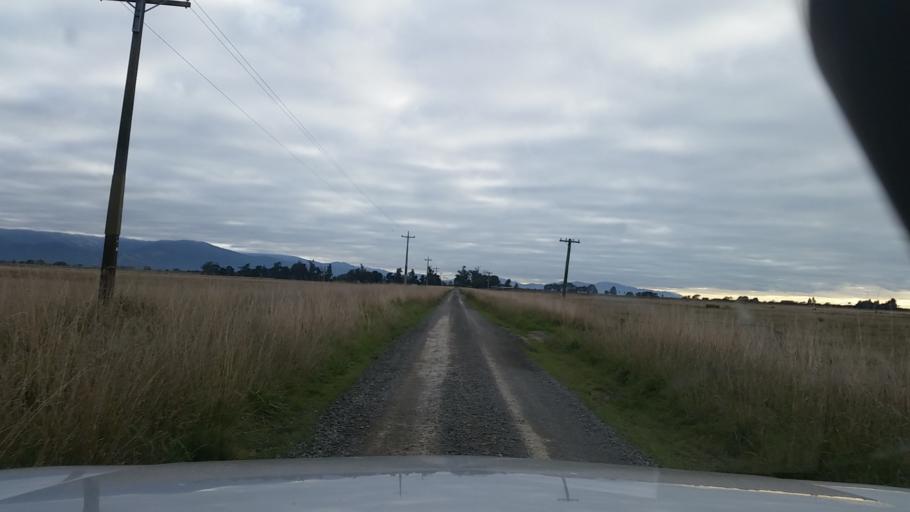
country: NZ
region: Marlborough
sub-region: Marlborough District
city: Blenheim
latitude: -41.5077
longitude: 174.0299
